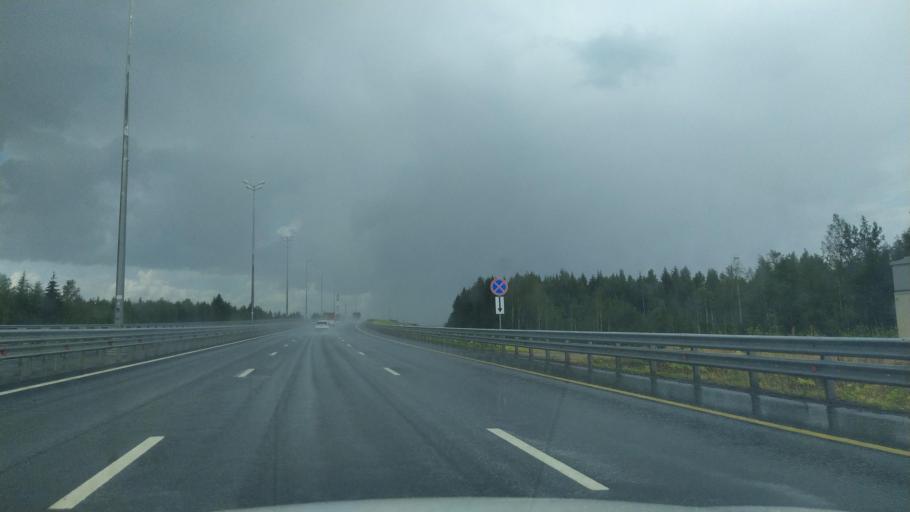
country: RU
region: Leningrad
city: Gatchina
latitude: 59.5275
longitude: 30.1331
